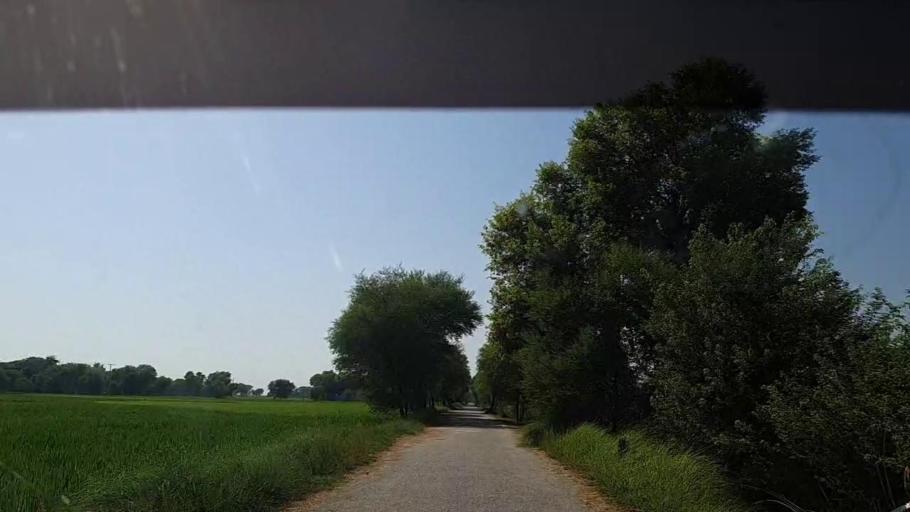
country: PK
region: Sindh
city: Ghauspur
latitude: 28.1740
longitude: 69.0526
